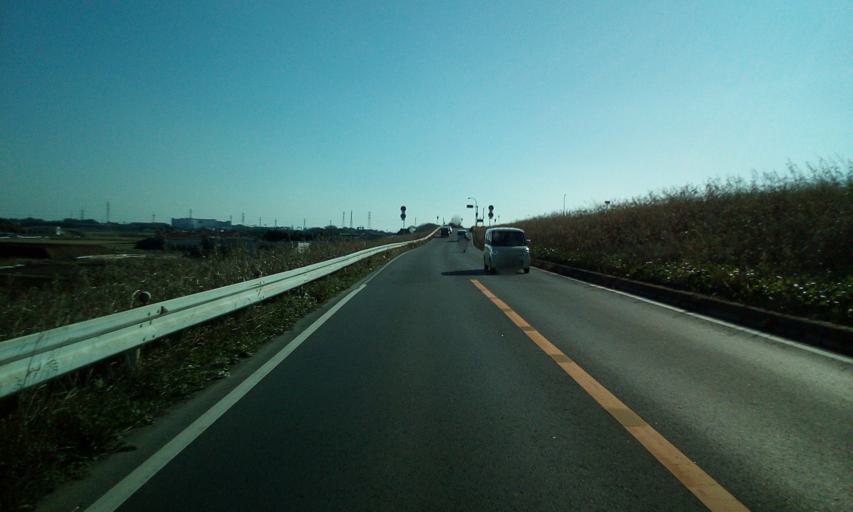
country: JP
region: Ibaraki
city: Sakai
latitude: 36.0836
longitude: 139.7822
